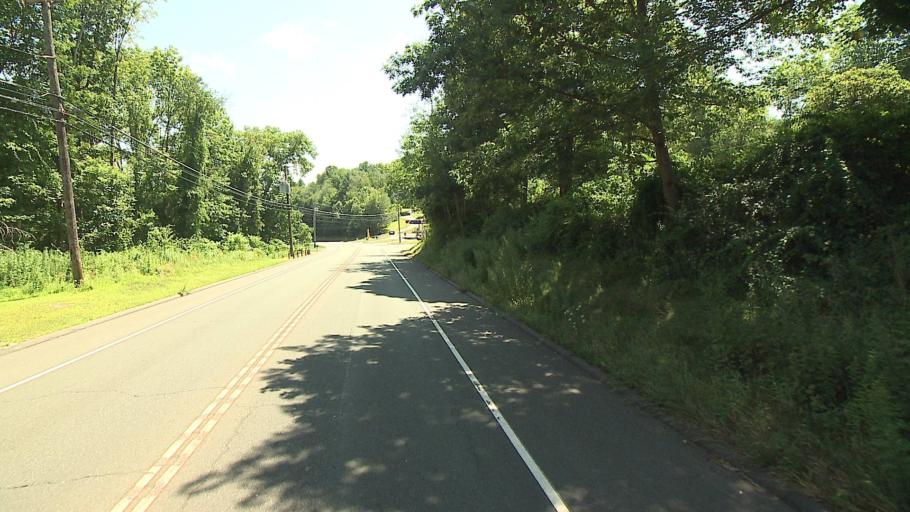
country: US
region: Connecticut
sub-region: Litchfield County
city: Northwest Harwinton
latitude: 41.7844
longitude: -73.0723
